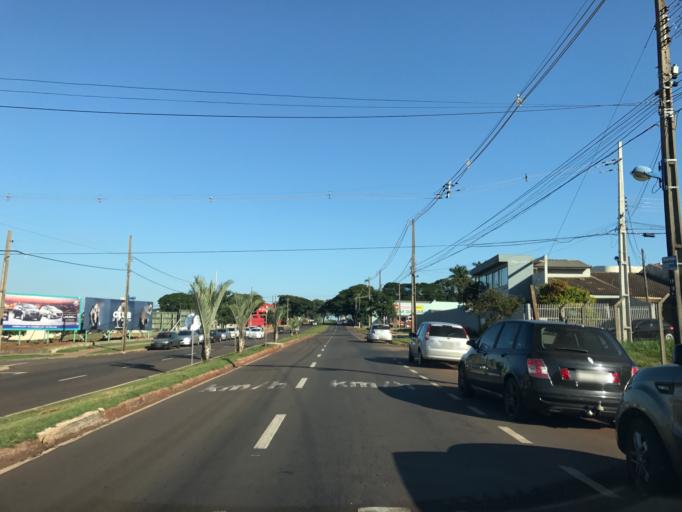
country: BR
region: Parana
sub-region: Maringa
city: Maringa
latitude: -23.4458
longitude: -51.9447
